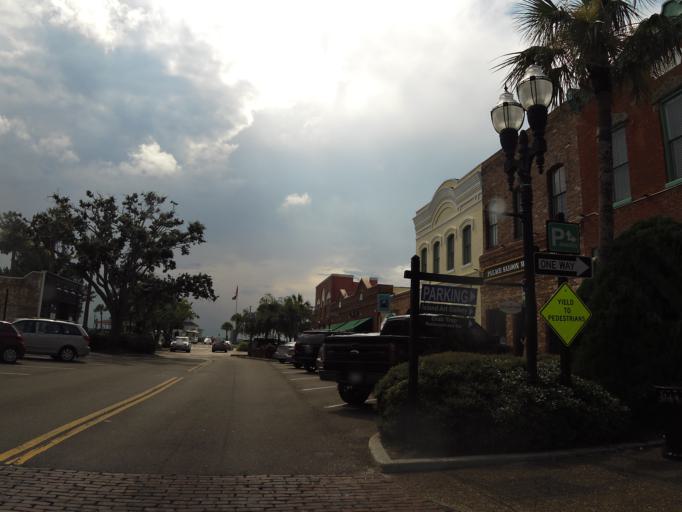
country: US
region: Florida
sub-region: Nassau County
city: Fernandina Beach
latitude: 30.6713
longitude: -81.4639
